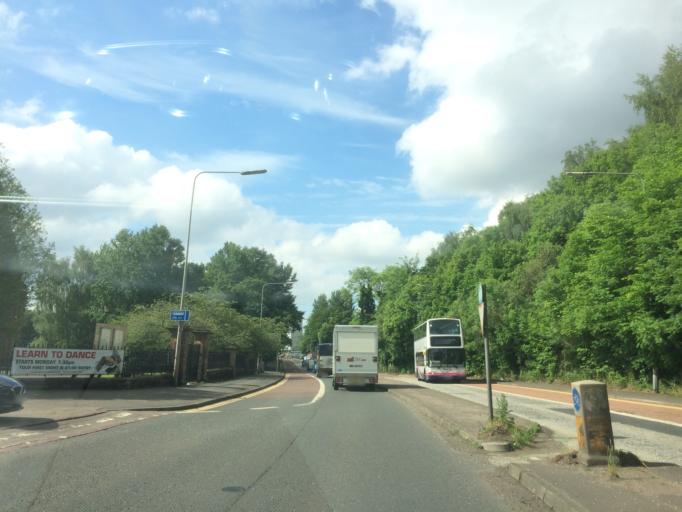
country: GB
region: Scotland
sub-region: East Renfrewshire
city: Giffnock
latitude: 55.8261
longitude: -4.2984
